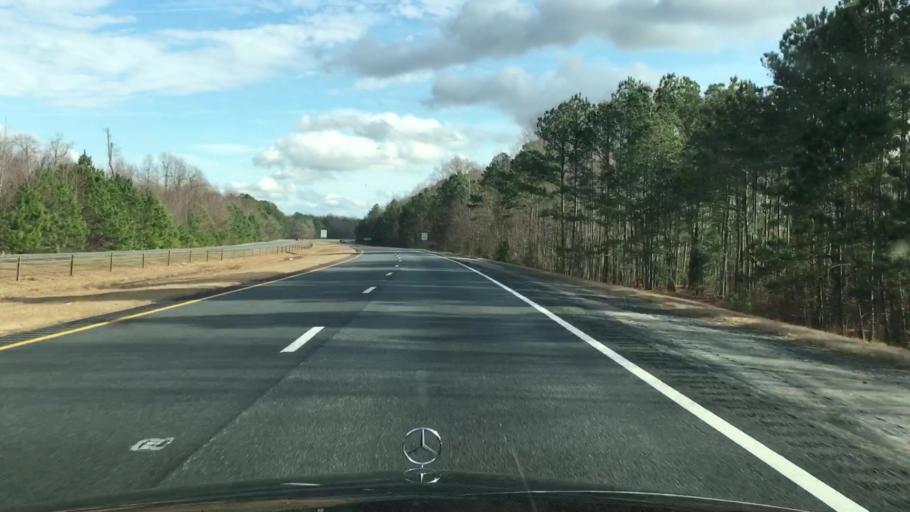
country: US
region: North Carolina
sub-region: Johnston County
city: Four Oaks
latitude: 35.3268
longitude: -78.4390
